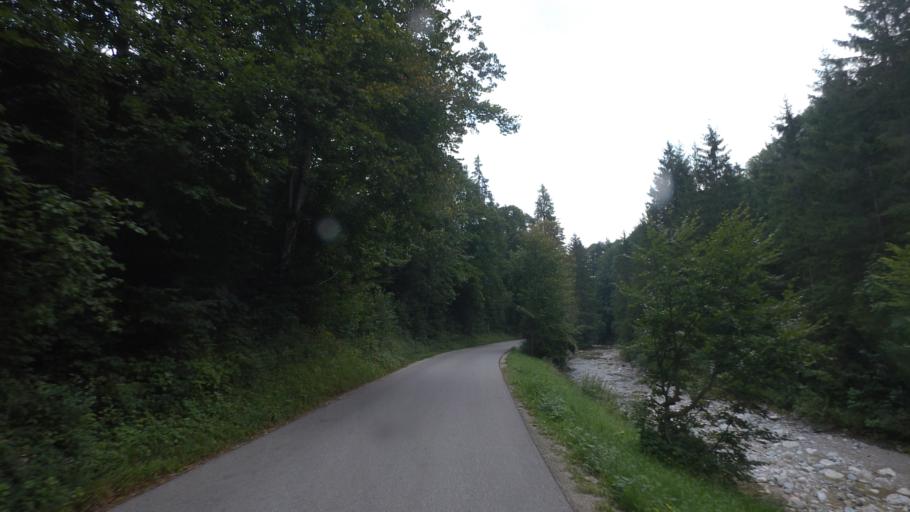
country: DE
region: Bavaria
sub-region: Upper Bavaria
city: Ruhpolding
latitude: 47.7345
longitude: 12.5990
